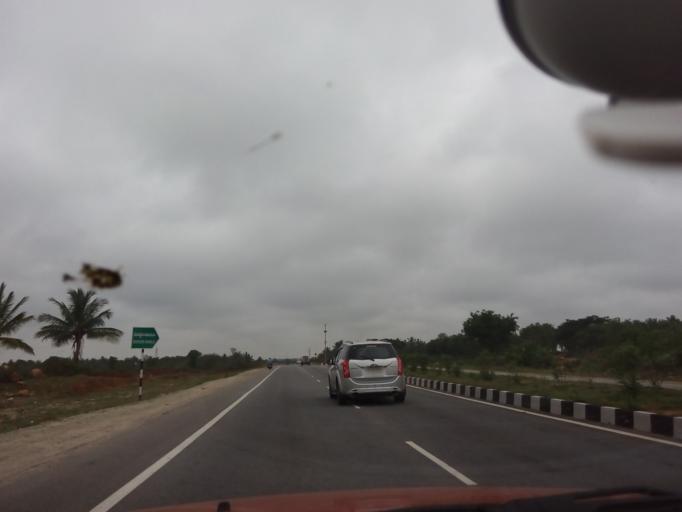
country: IN
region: Karnataka
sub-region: Hassan
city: Shravanabelagola
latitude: 12.9347
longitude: 76.5340
